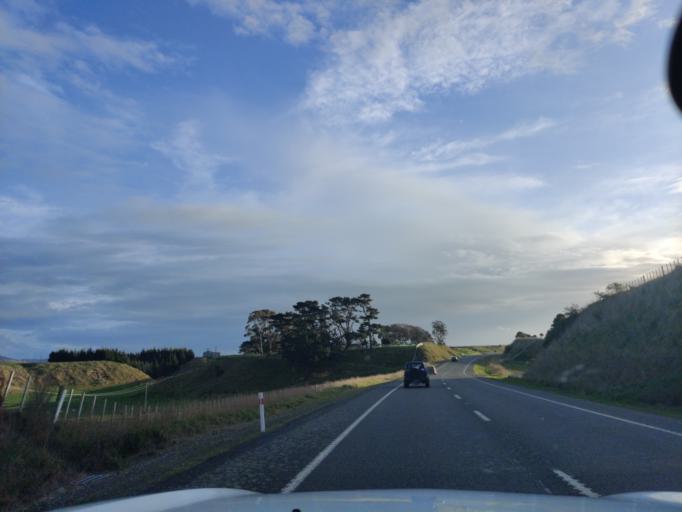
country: NZ
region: Manawatu-Wanganui
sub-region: Horowhenua District
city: Foxton
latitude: -40.5125
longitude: 175.4643
